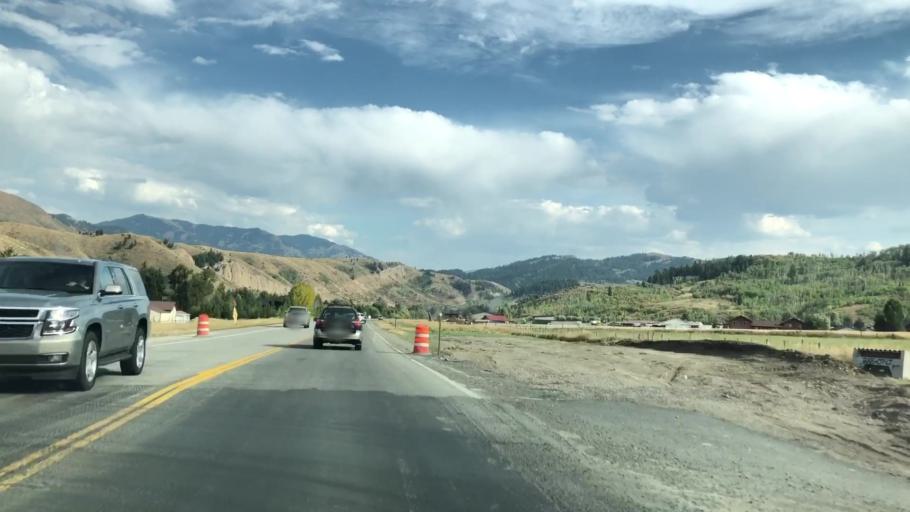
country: US
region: Wyoming
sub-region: Teton County
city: South Park
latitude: 43.3706
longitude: -110.7396
